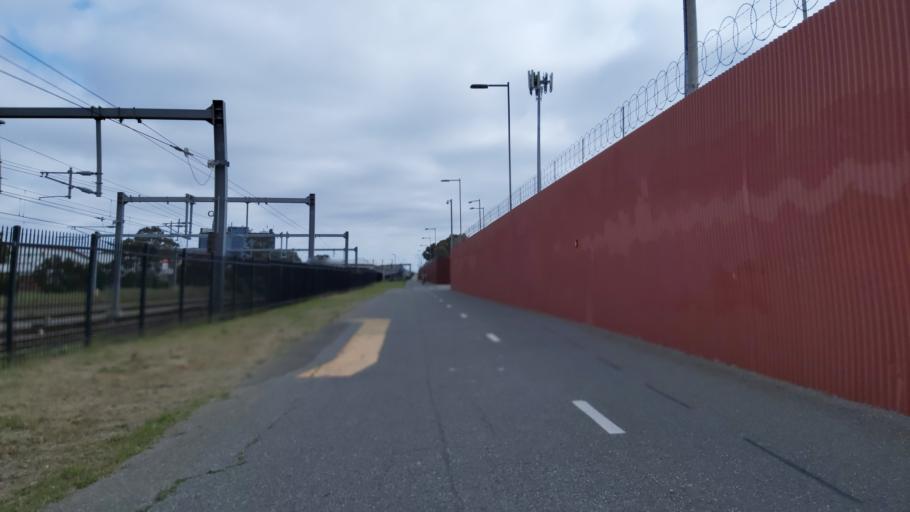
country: AU
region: South Australia
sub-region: Unley
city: Wayville
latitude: -34.9462
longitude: 138.5840
